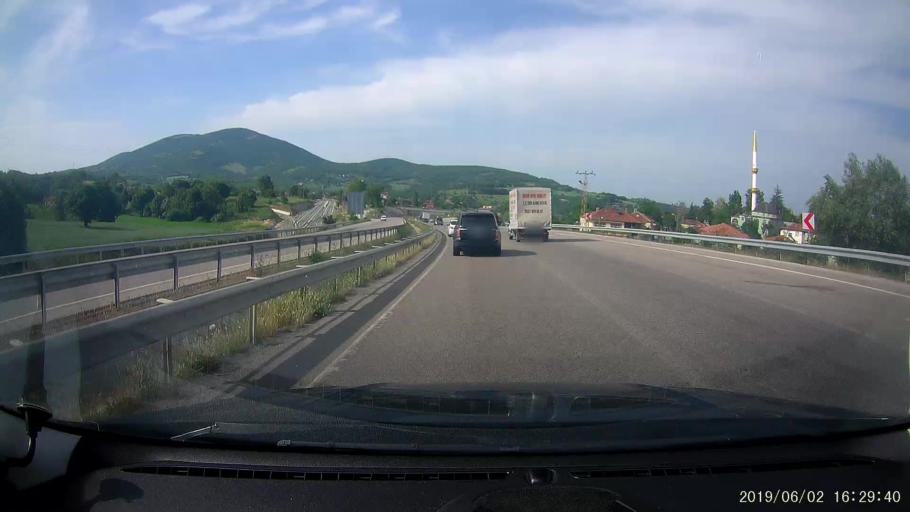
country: TR
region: Samsun
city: Ladik
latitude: 41.0156
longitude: 35.8719
